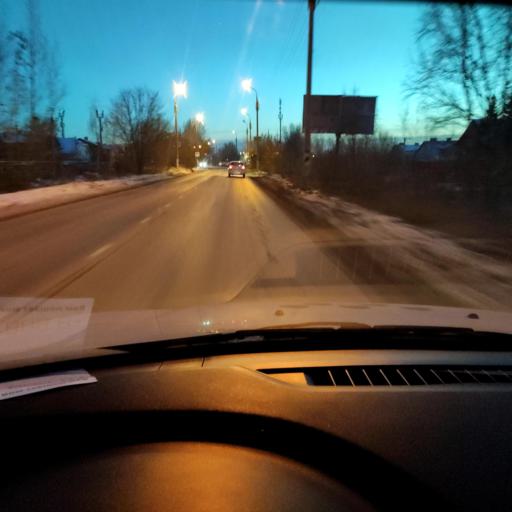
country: RU
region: Samara
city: Tol'yatti
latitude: 53.5587
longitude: 49.3945
